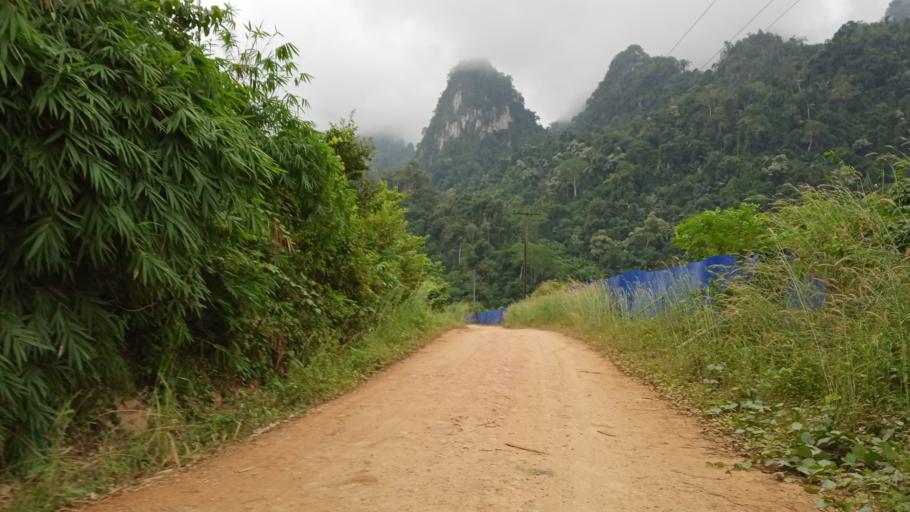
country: LA
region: Xiangkhoang
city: Phonsavan
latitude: 19.0899
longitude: 103.0063
